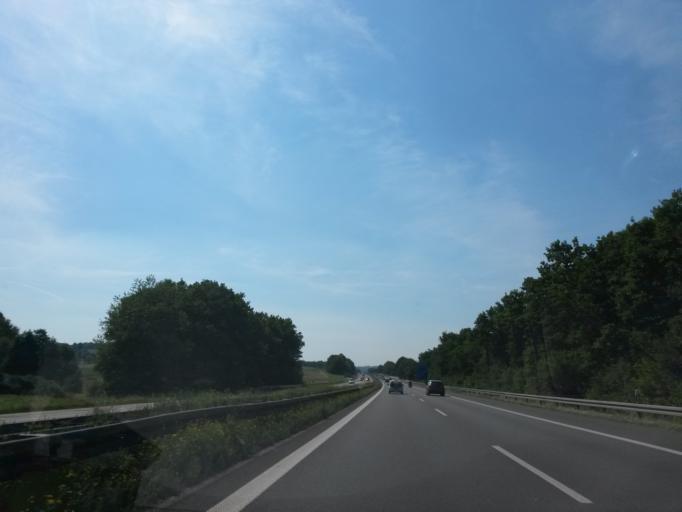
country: DE
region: Bavaria
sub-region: Regierungsbezirk Unterfranken
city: Geiselwind
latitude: 49.7686
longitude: 10.4923
